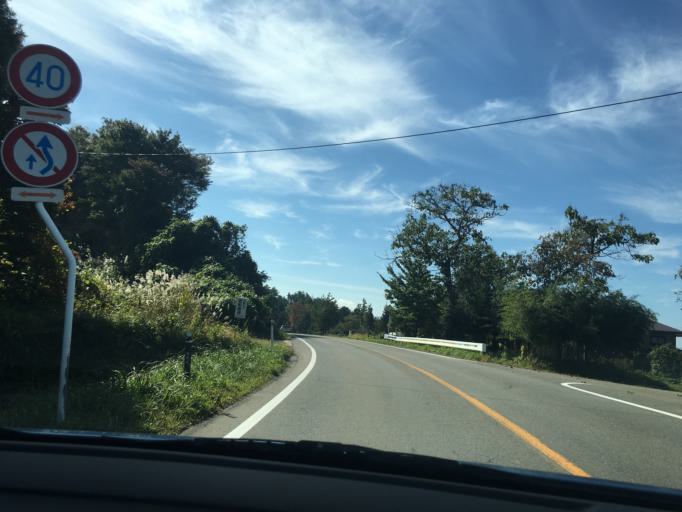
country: JP
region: Fukushima
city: Kitakata
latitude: 37.5386
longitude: 139.9647
